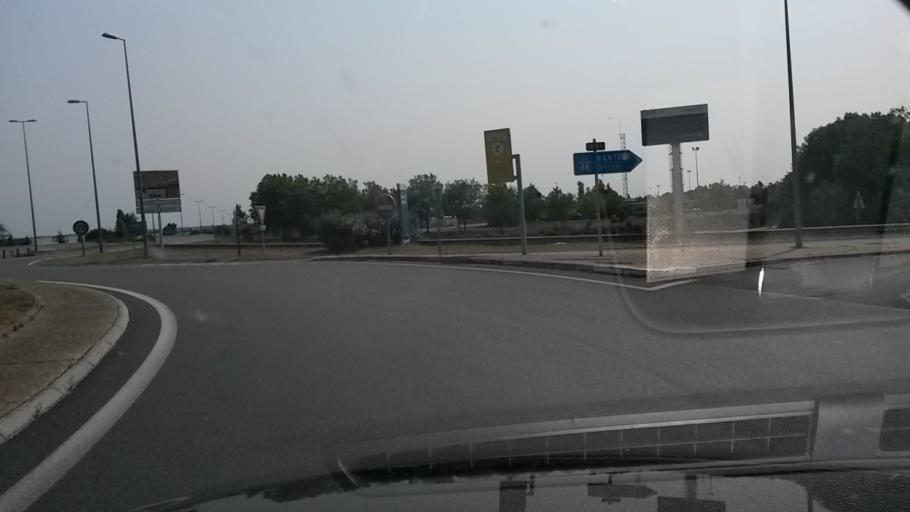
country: FR
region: Pays de la Loire
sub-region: Departement de la Loire-Atlantique
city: Saint-Gereon
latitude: 47.4029
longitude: -1.1912
